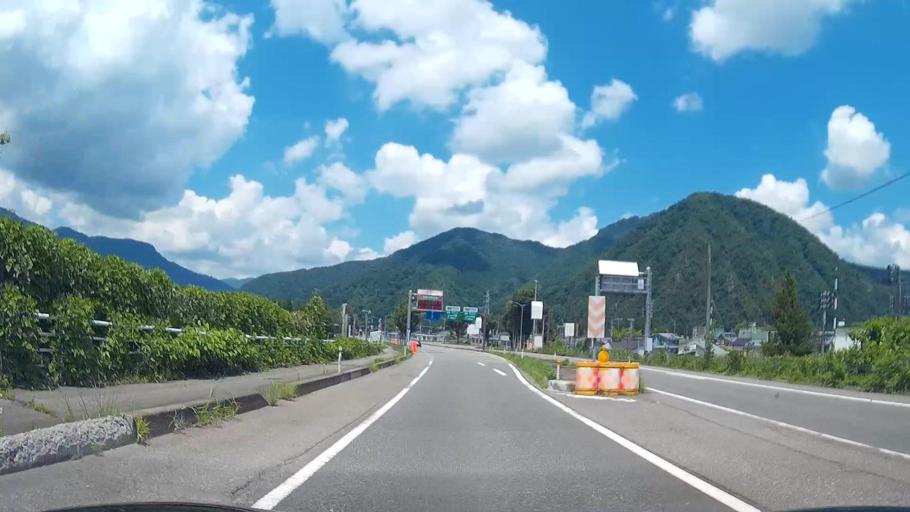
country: JP
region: Niigata
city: Shiozawa
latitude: 36.9287
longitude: 138.8238
